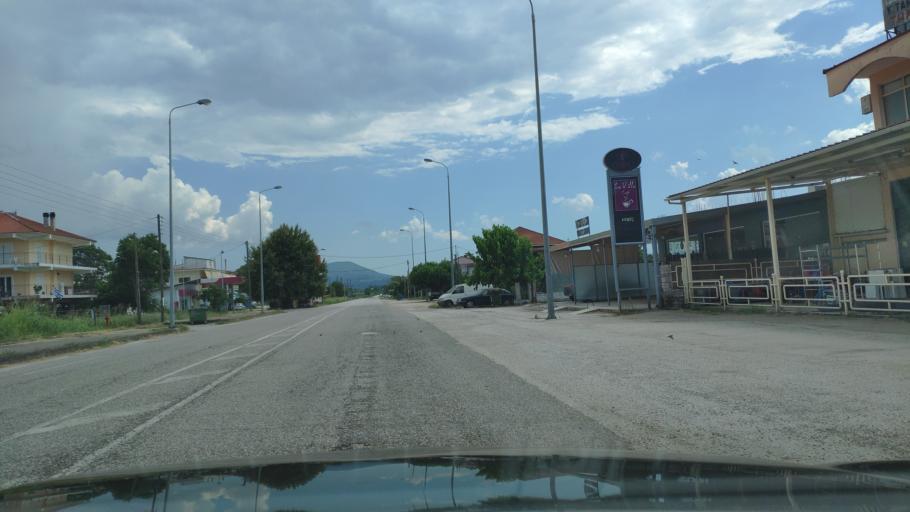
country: GR
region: West Greece
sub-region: Nomos Aitolias kai Akarnanias
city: Krikellos
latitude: 38.9469
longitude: 21.1763
